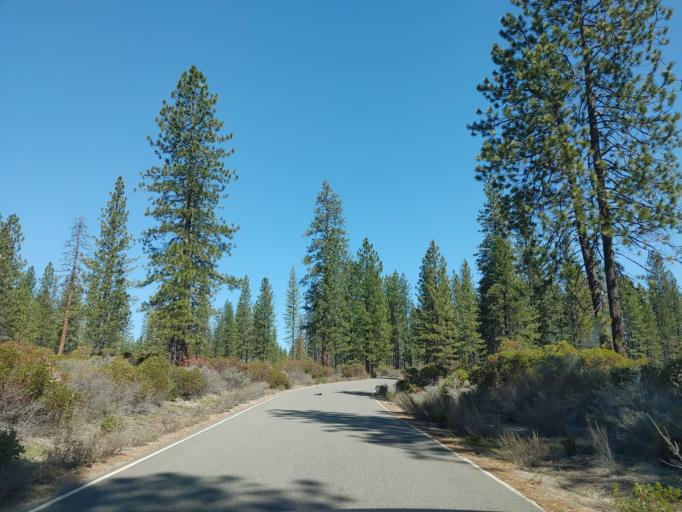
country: US
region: California
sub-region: Siskiyou County
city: McCloud
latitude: 41.2464
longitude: -122.0283
